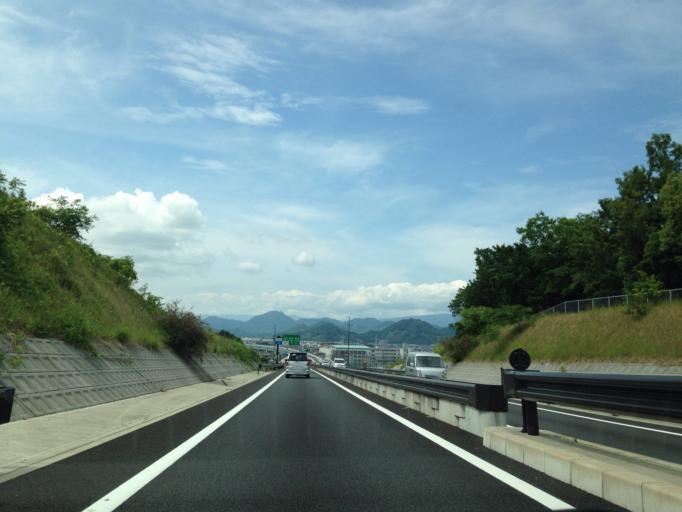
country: JP
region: Shizuoka
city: Mishima
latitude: 35.1009
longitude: 138.9481
